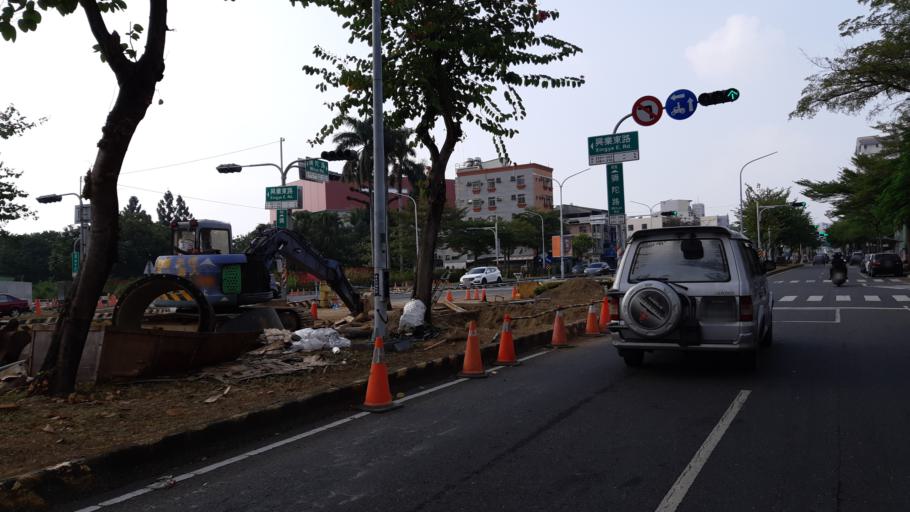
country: TW
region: Taiwan
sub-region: Chiayi
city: Jiayi Shi
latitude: 23.4706
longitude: 120.4650
